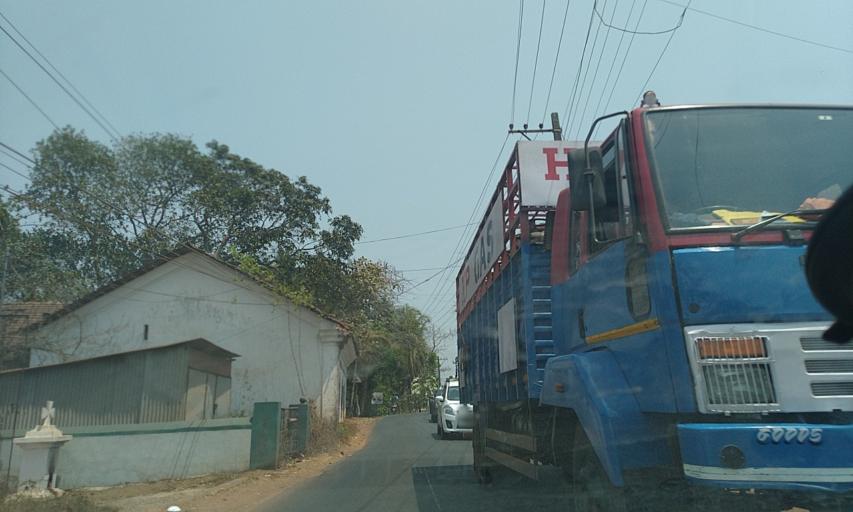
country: IN
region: Goa
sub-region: North Goa
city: Saligao
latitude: 15.5459
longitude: 73.8038
